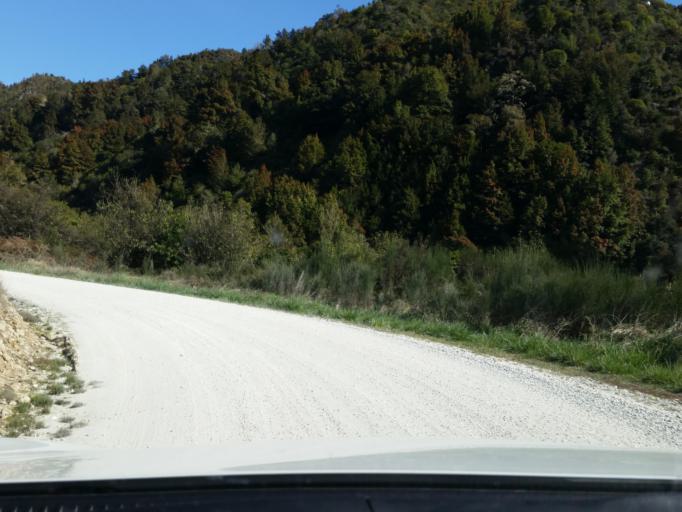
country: NZ
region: West Coast
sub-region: Buller District
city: Westport
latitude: -41.7682
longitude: 172.2365
